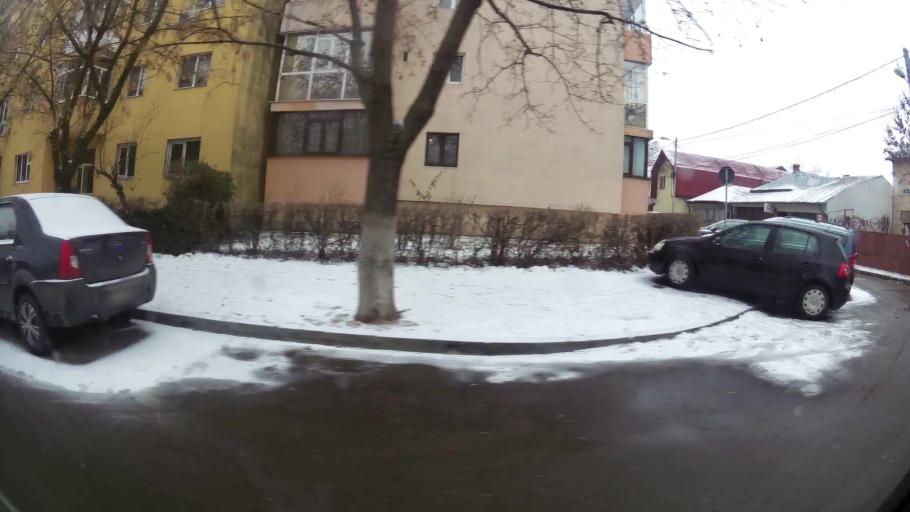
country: RO
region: Prahova
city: Ploiesti
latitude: 44.9394
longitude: 26.0004
